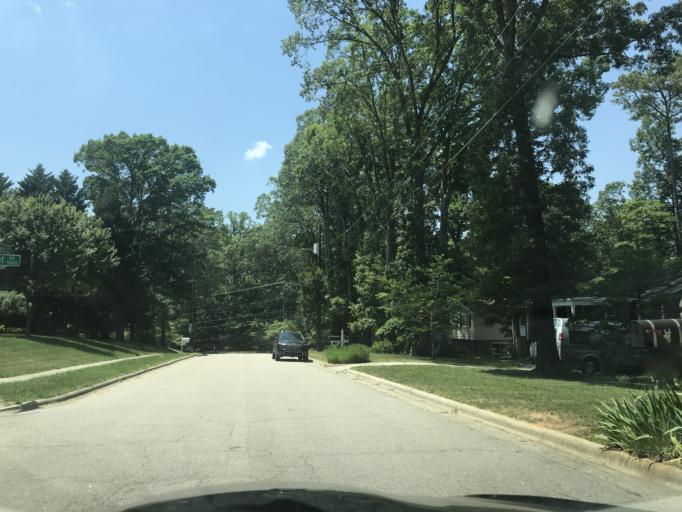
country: US
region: North Carolina
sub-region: Wake County
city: West Raleigh
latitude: 35.8498
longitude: -78.6194
